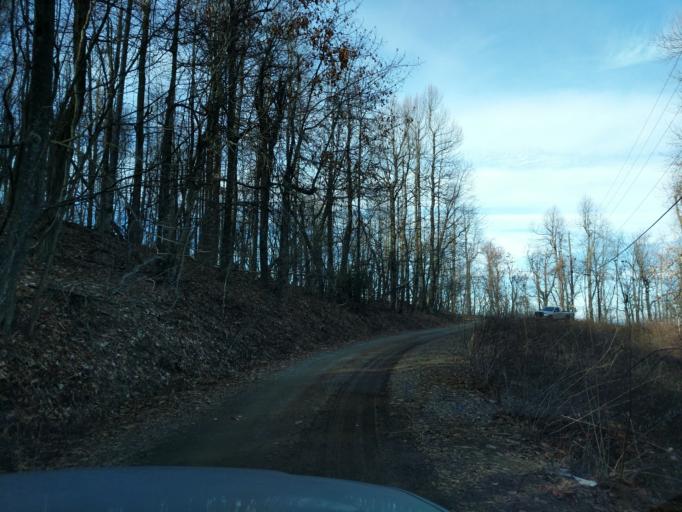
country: US
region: North Carolina
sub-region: Polk County
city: Columbus
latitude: 35.2740
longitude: -82.2326
